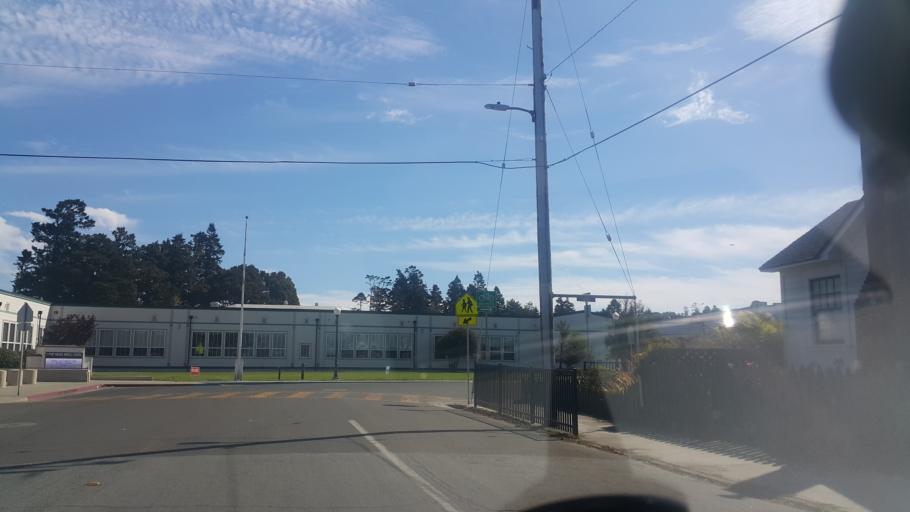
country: US
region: California
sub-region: Mendocino County
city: Fort Bragg
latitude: 39.4479
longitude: -123.7986
